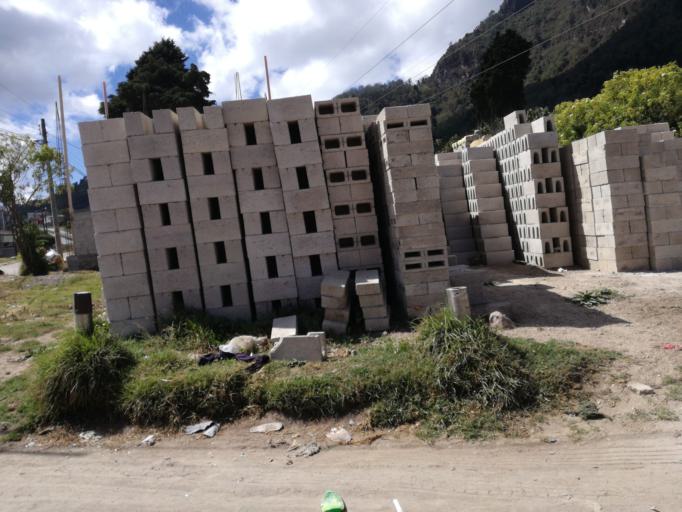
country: GT
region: Quetzaltenango
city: Almolonga
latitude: 14.7839
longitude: -91.5361
